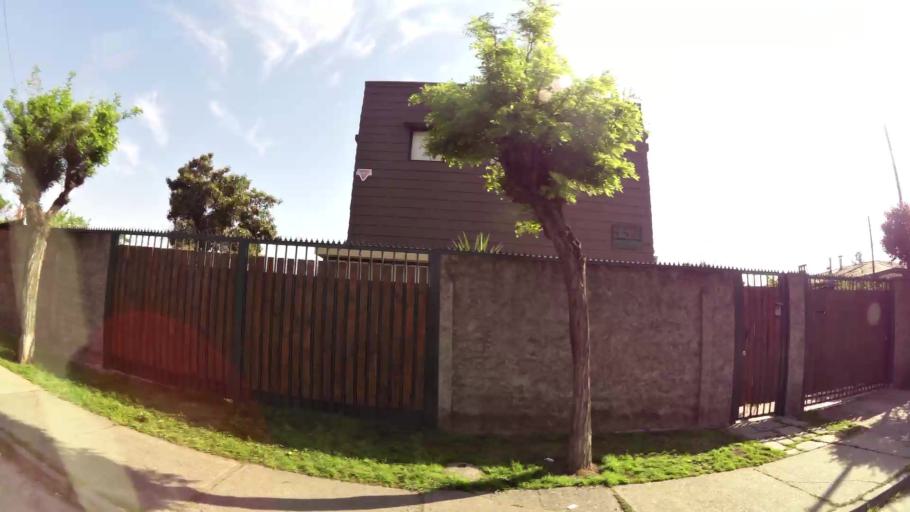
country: CL
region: Santiago Metropolitan
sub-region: Provincia de Santiago
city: La Pintana
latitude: -33.5602
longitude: -70.5974
